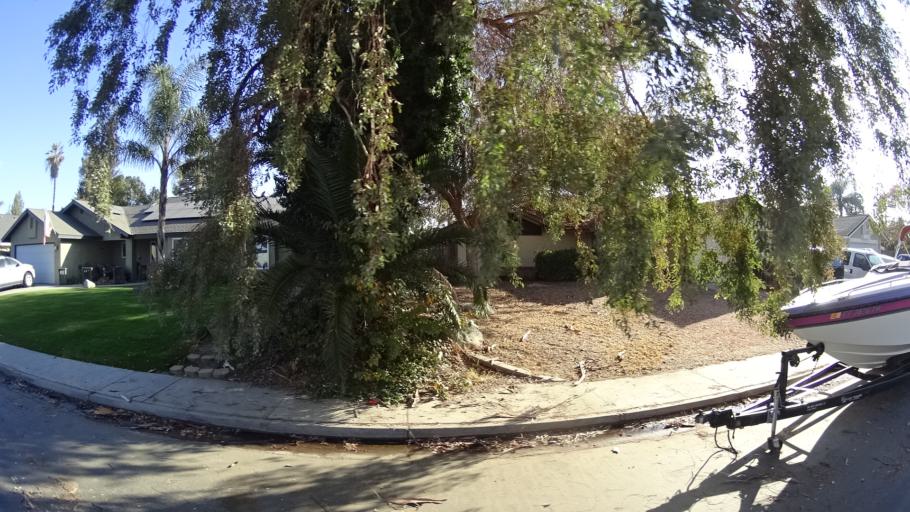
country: US
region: California
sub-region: Kern County
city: Rosedale
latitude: 35.3491
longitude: -119.1472
